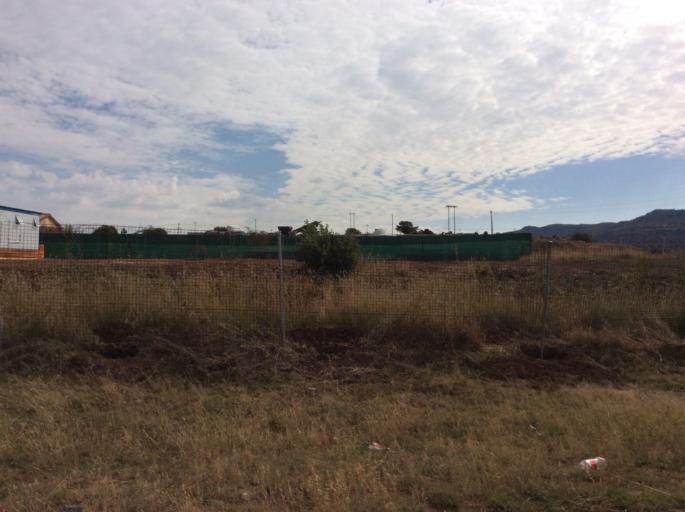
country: LS
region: Mafeteng
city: Mafeteng
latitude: -29.7229
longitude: 27.0137
